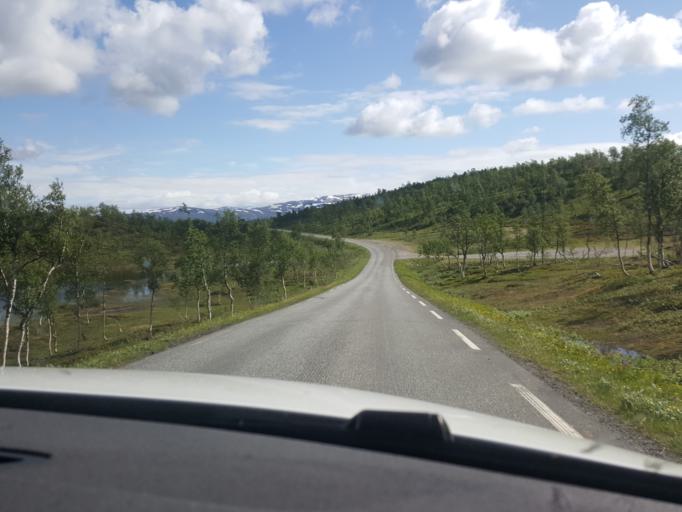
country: NO
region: Nordland
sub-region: Saltdal
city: Rognan
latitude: 67.0345
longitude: 15.1871
